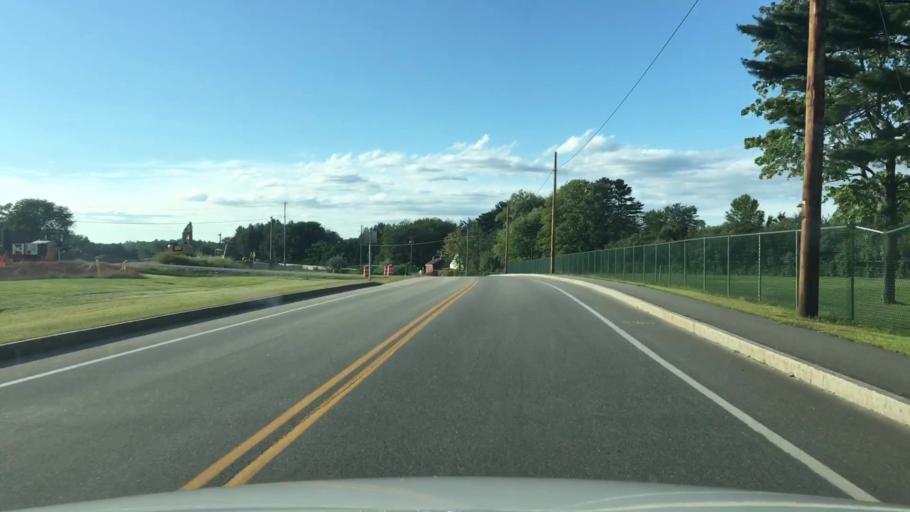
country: US
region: Maine
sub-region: York County
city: Eliot
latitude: 43.1217
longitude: -70.8289
